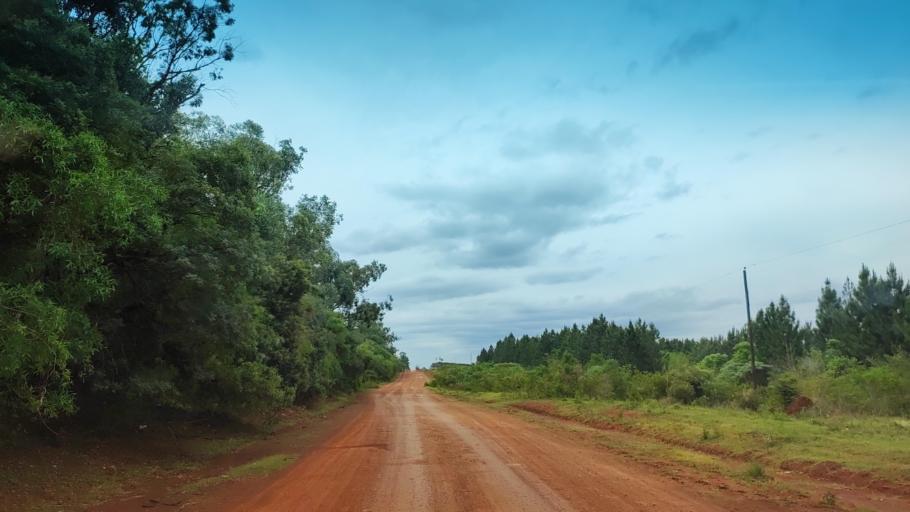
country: AR
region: Misiones
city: Garupa
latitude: -27.4934
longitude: -55.9708
